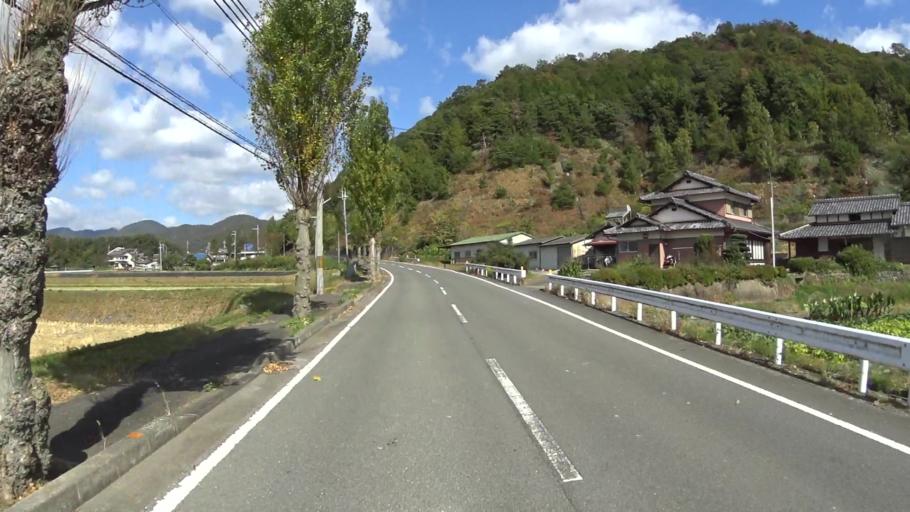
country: JP
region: Kyoto
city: Kameoka
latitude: 35.0808
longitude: 135.5659
